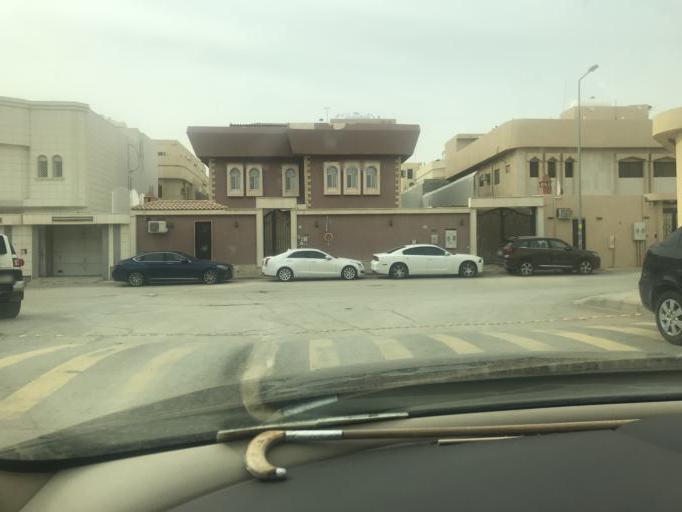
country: SA
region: Ar Riyad
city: Riyadh
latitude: 24.7512
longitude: 46.7616
